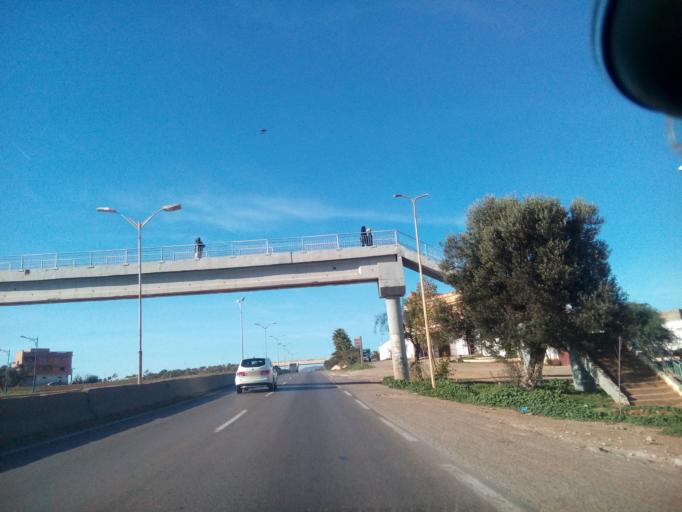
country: DZ
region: Oran
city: Ain el Bya
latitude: 35.7966
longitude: -0.3791
